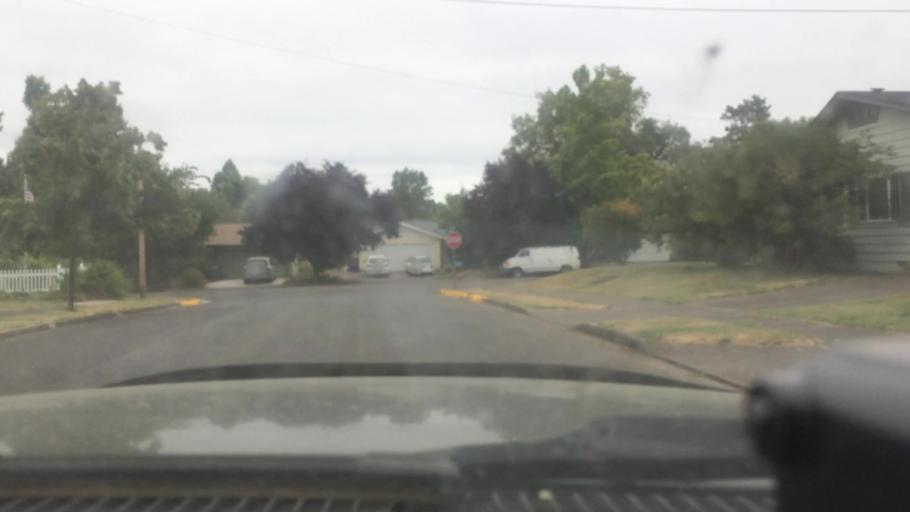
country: US
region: Oregon
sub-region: Lane County
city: Eugene
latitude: 44.0309
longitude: -123.1129
